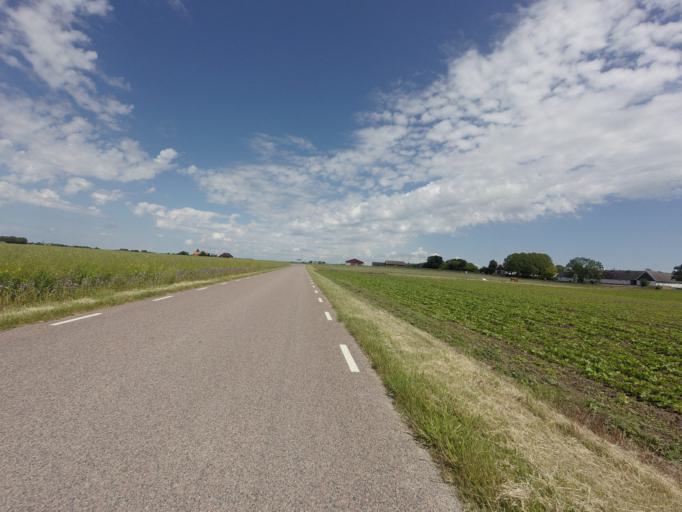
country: SE
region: Skane
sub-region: Trelleborgs Kommun
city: Skare
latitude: 55.4230
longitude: 13.1050
